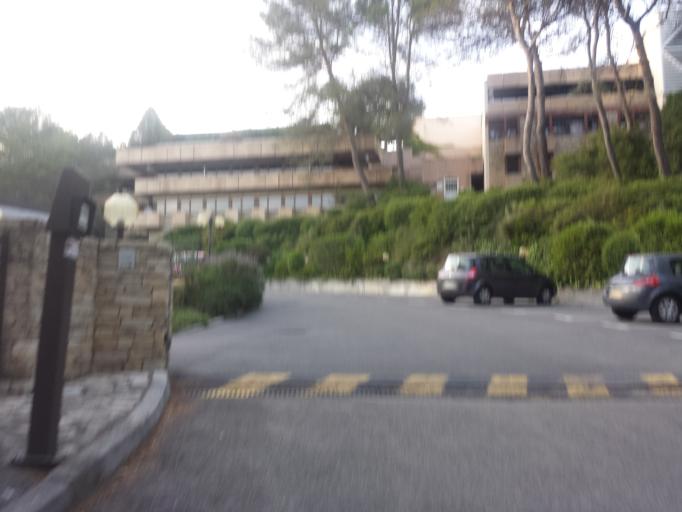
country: FR
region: Provence-Alpes-Cote d'Azur
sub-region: Departement des Alpes-Maritimes
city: Vallauris
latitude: 43.6143
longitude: 7.0546
